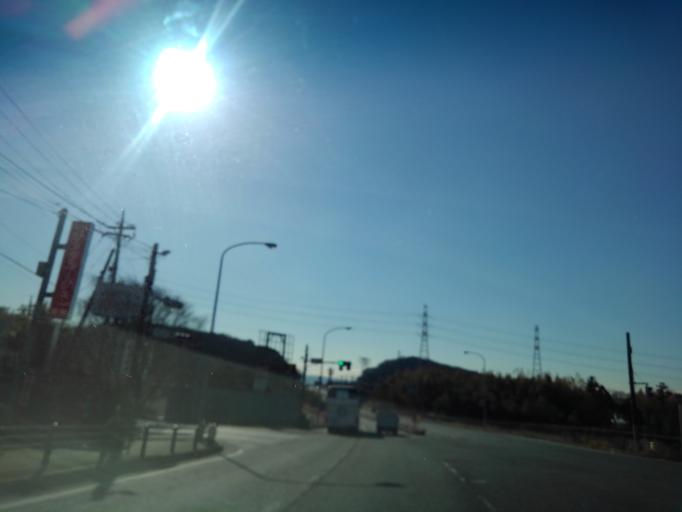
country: JP
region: Chiba
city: Kisarazu
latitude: 35.3436
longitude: 139.9207
